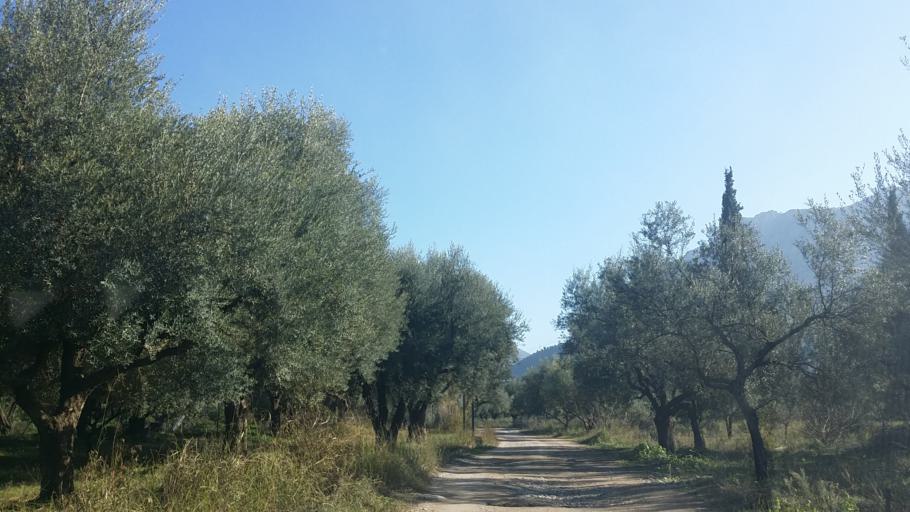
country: GR
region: West Greece
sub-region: Nomos Achaias
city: Temeni
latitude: 38.1927
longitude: 22.1857
